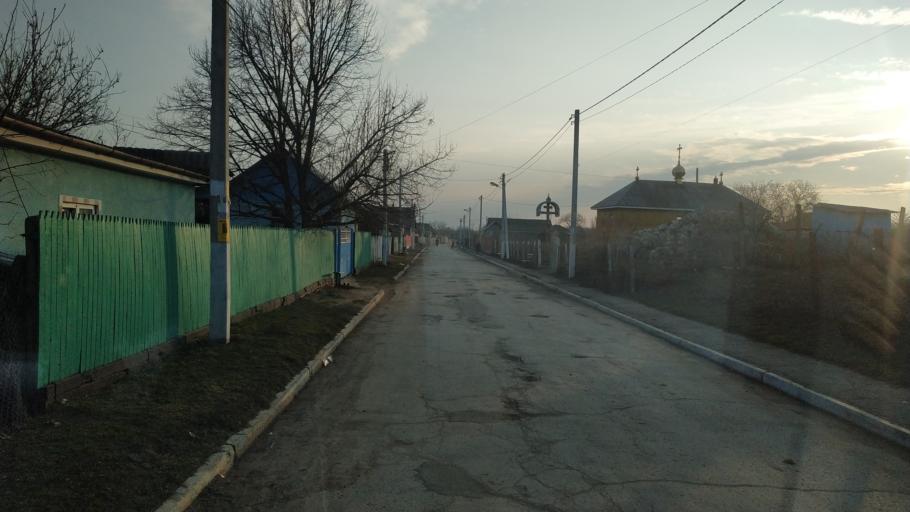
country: MD
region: Hincesti
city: Dancu
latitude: 46.7180
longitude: 28.3523
